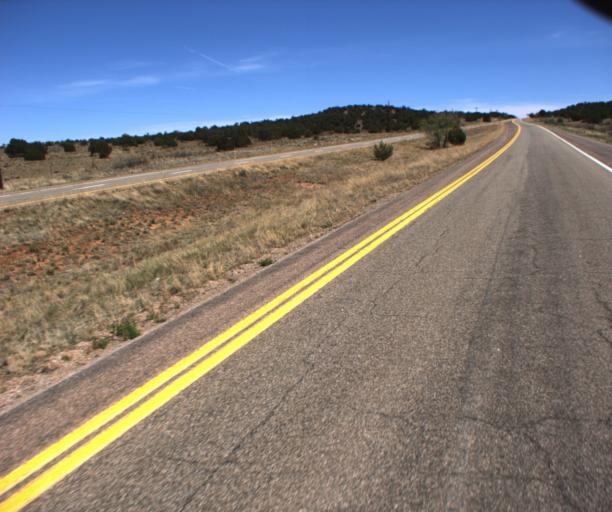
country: US
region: Arizona
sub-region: Mohave County
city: Peach Springs
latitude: 35.5291
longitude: -113.2281
